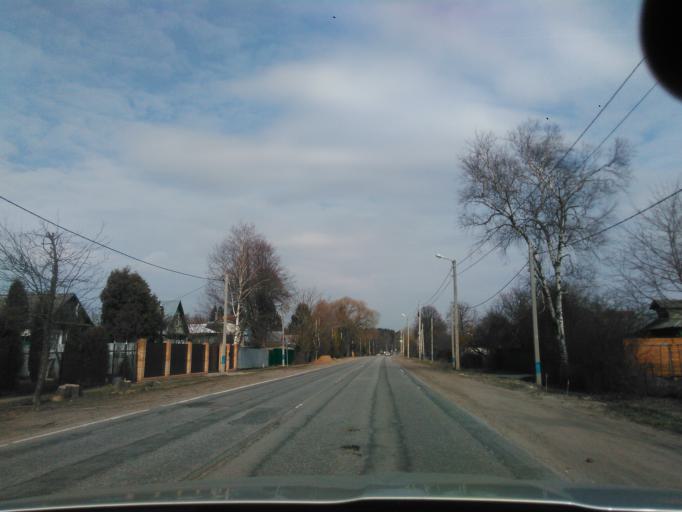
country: RU
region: Moskovskaya
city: Marfino
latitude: 56.0503
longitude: 37.5346
